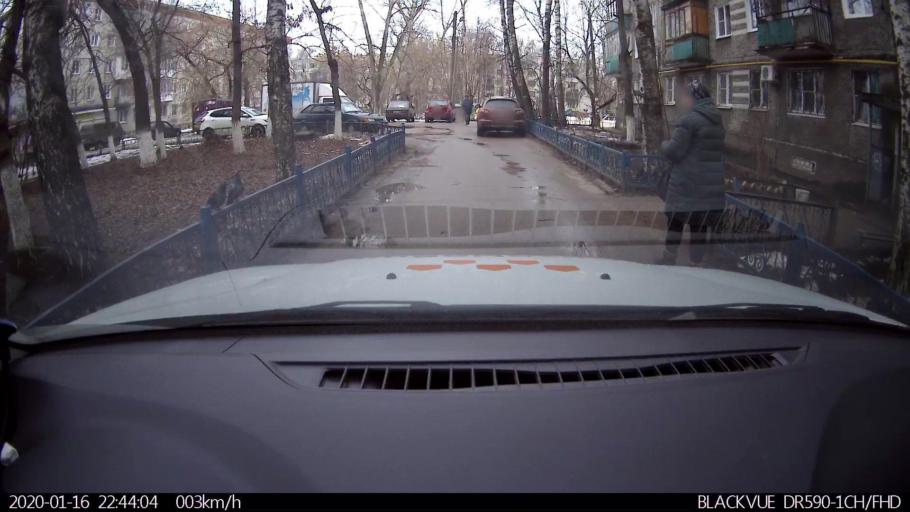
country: RU
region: Nizjnij Novgorod
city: Nizhniy Novgorod
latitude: 56.2831
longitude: 43.9236
